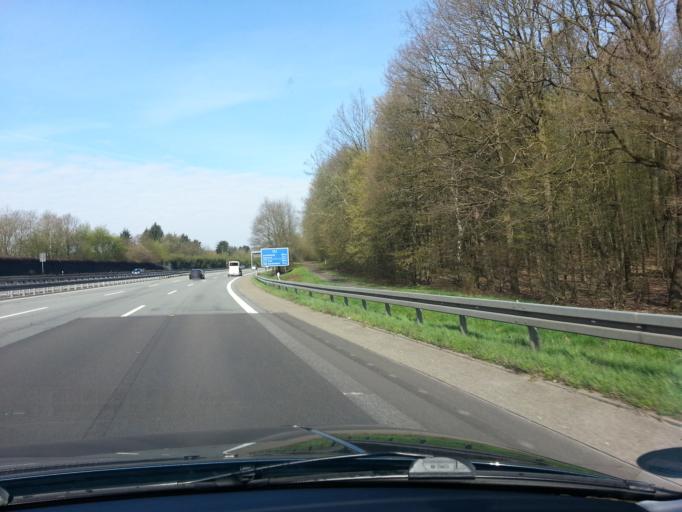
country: DE
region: Saarland
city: Spiesen-Elversberg
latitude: 49.3212
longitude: 7.1420
